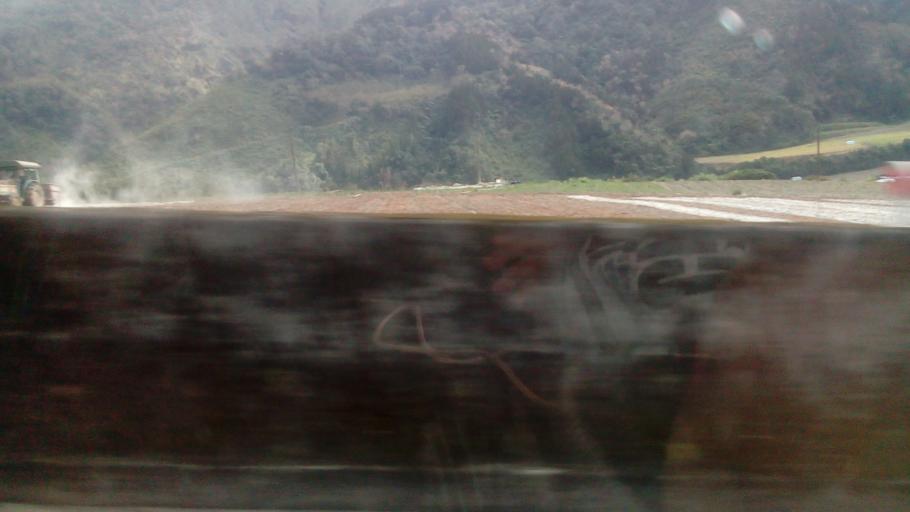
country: TW
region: Taiwan
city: Daxi
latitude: 24.4597
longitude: 121.3944
